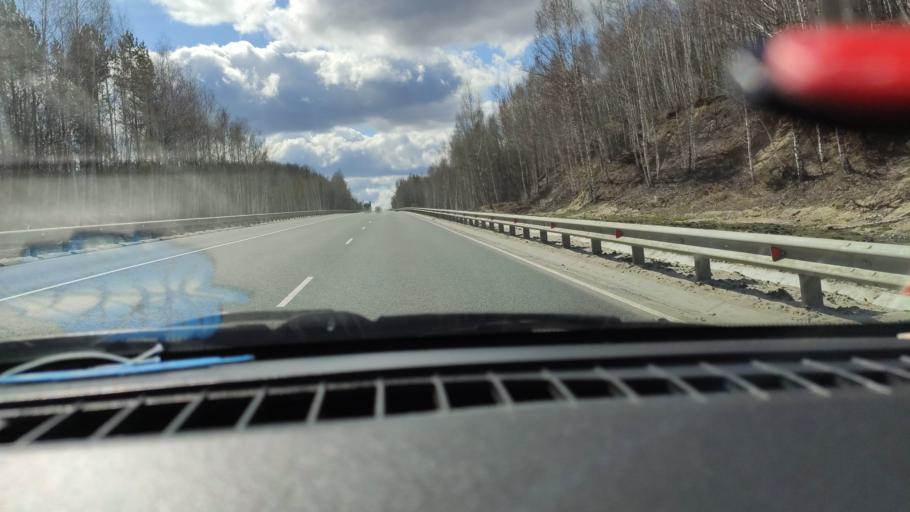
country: RU
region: Saratov
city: Khvalynsk
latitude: 52.4971
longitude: 48.0142
